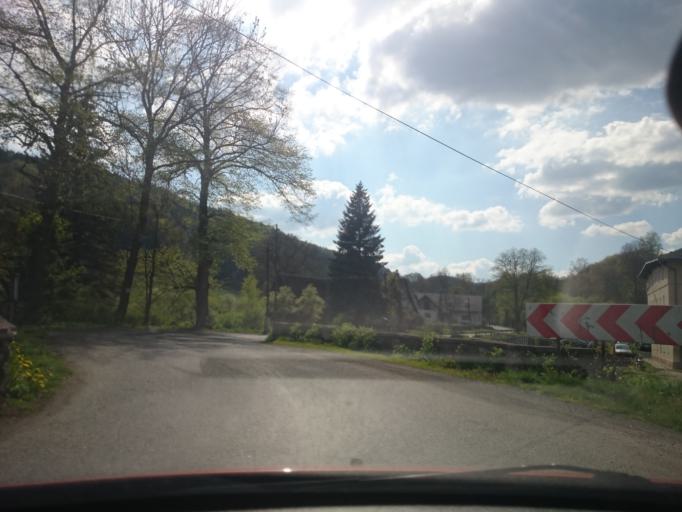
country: PL
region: Lower Silesian Voivodeship
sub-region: Powiat klodzki
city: Bystrzyca Klodzka
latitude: 50.3052
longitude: 16.6078
